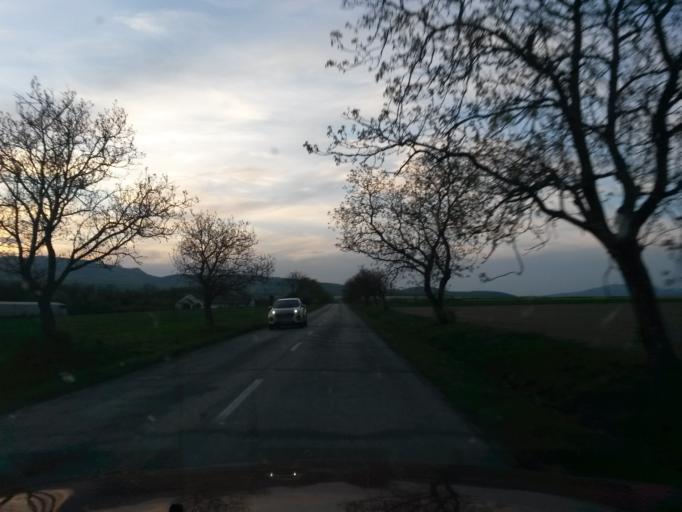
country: HU
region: Borsod-Abauj-Zemplen
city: Satoraljaujhely
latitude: 48.5421
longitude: 21.5669
